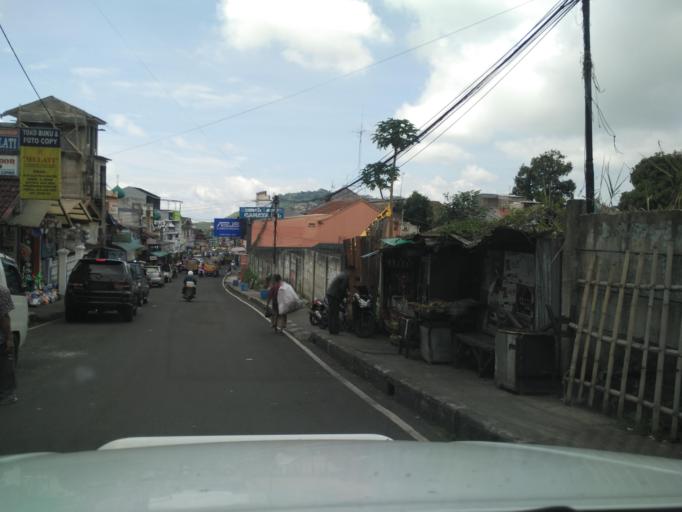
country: ID
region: West Java
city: Caringin
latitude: -6.7277
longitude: 107.0403
